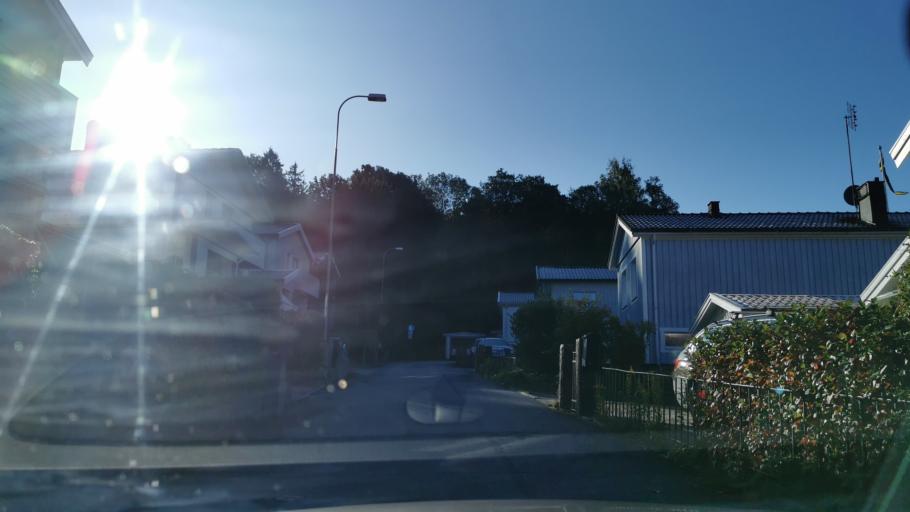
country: SE
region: Vaestra Goetaland
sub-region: Goteborg
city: Eriksbo
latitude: 57.7279
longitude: 12.0556
